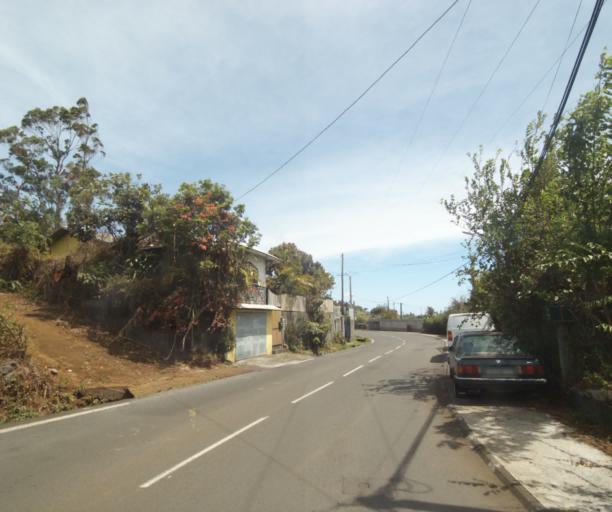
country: RE
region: Reunion
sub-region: Reunion
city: Trois-Bassins
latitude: -21.0611
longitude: 55.3081
